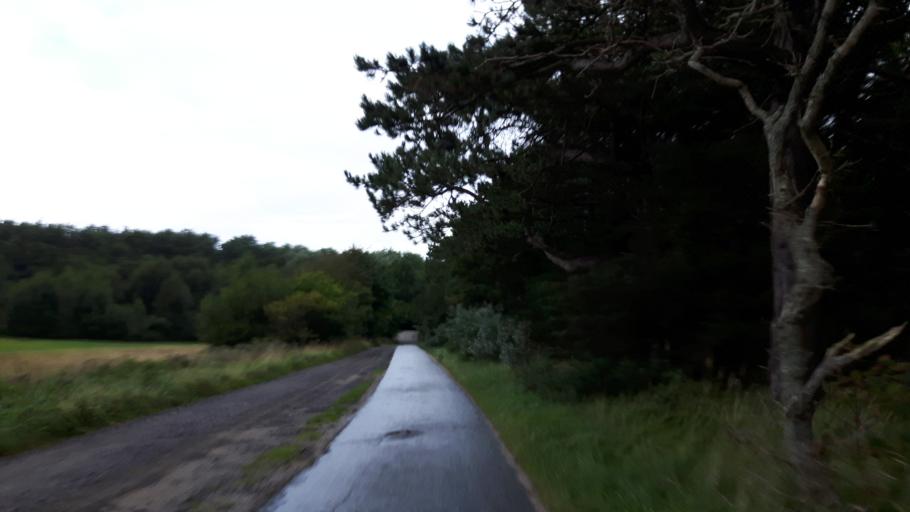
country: NL
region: Friesland
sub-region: Gemeente Ameland
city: Nes
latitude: 53.4519
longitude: 5.7570
